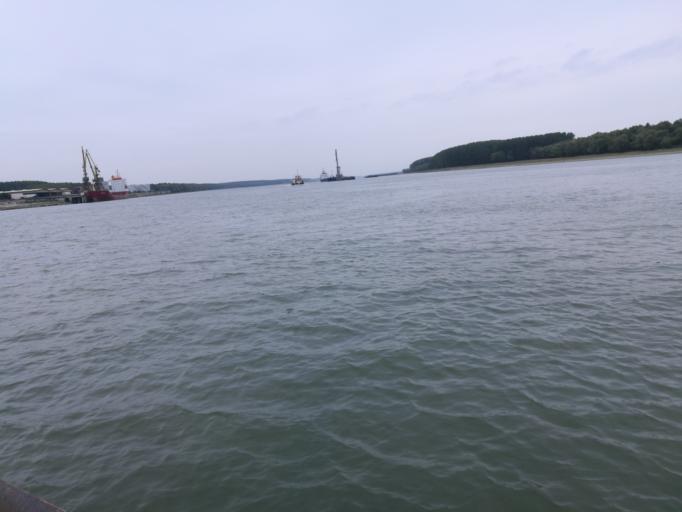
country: RO
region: Braila
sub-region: Municipiul Braila
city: Braila
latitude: 45.2881
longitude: 27.9947
